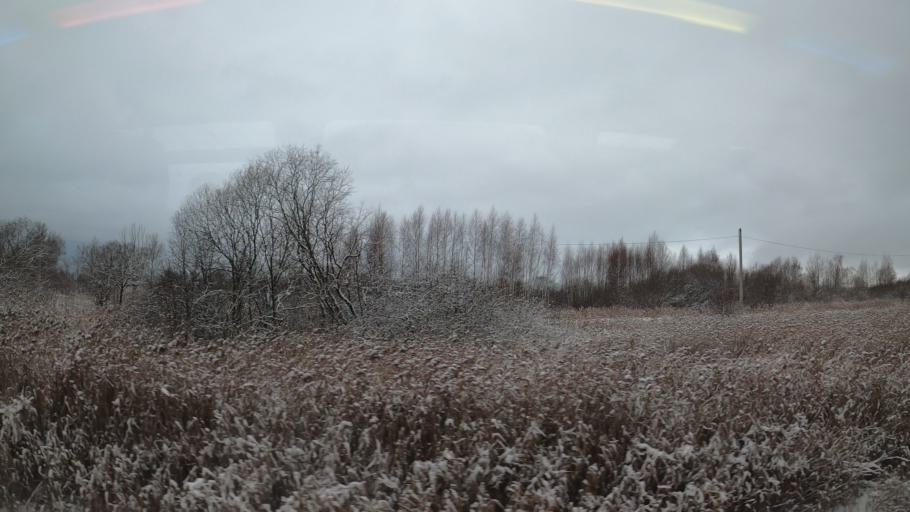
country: RU
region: Jaroslavl
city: Pereslavl'-Zalesskiy
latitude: 56.7265
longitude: 38.9037
